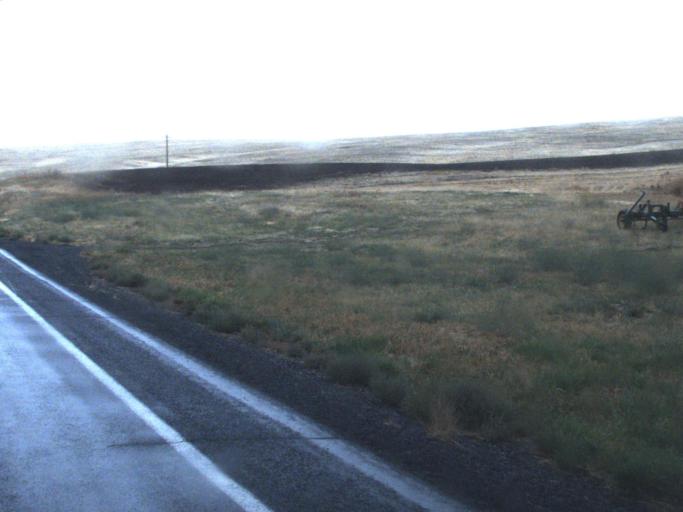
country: US
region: Washington
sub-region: Whitman County
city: Colfax
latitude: 47.1052
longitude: -117.6218
